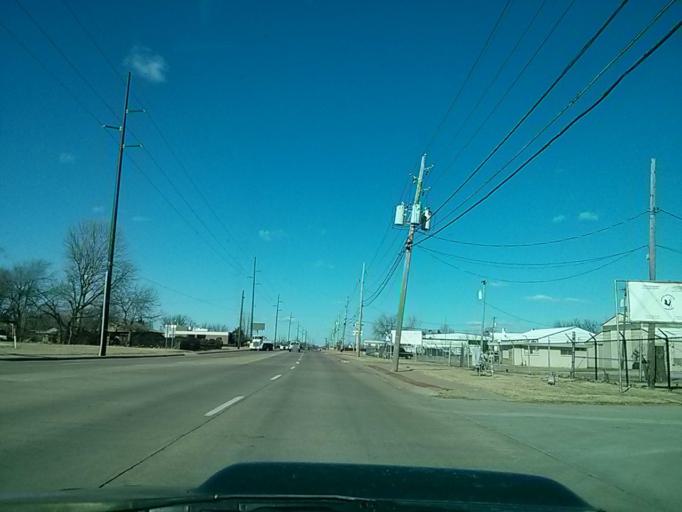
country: US
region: Oklahoma
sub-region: Tulsa County
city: Turley
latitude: 36.1995
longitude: -95.9581
